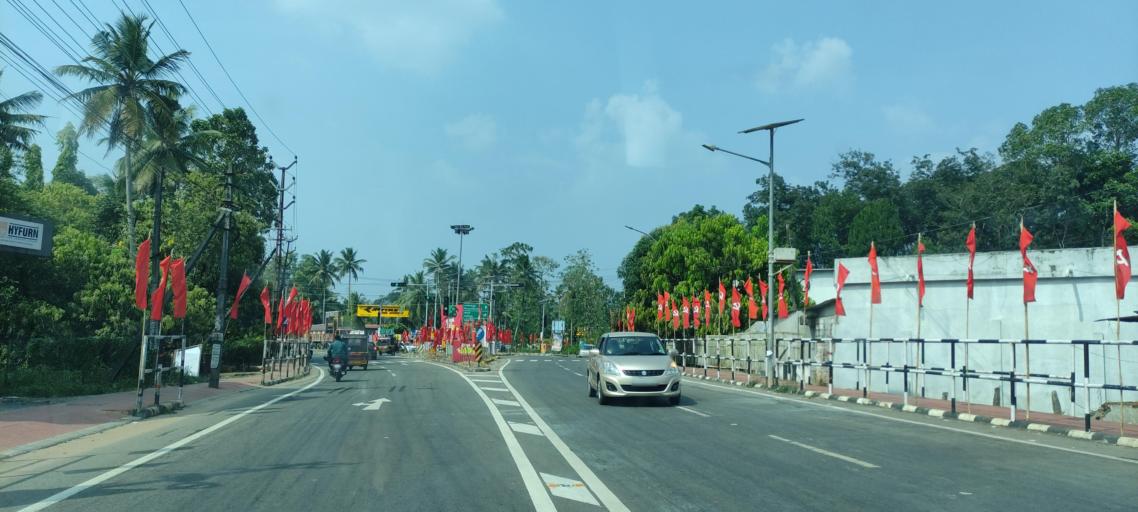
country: IN
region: Kerala
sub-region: Pattanamtitta
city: Adur
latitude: 9.1456
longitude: 76.7324
